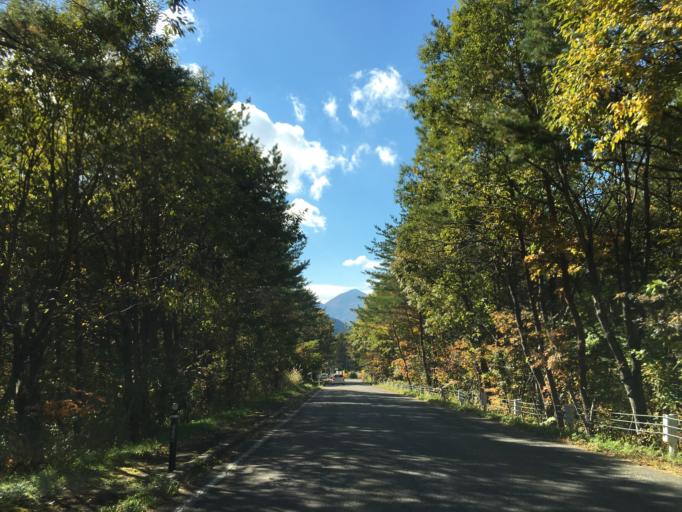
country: JP
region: Fukushima
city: Inawashiro
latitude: 37.6132
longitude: 140.2251
